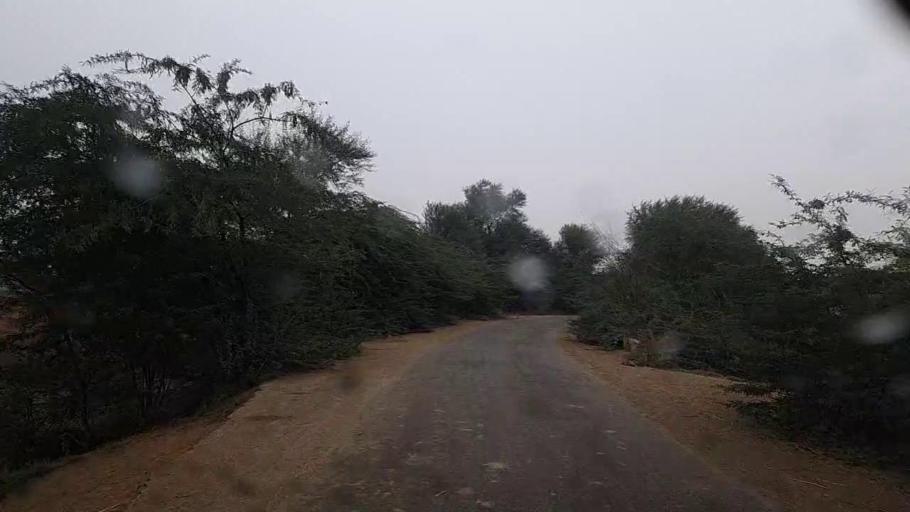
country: PK
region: Sindh
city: Ranipur
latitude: 27.2657
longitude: 68.5693
